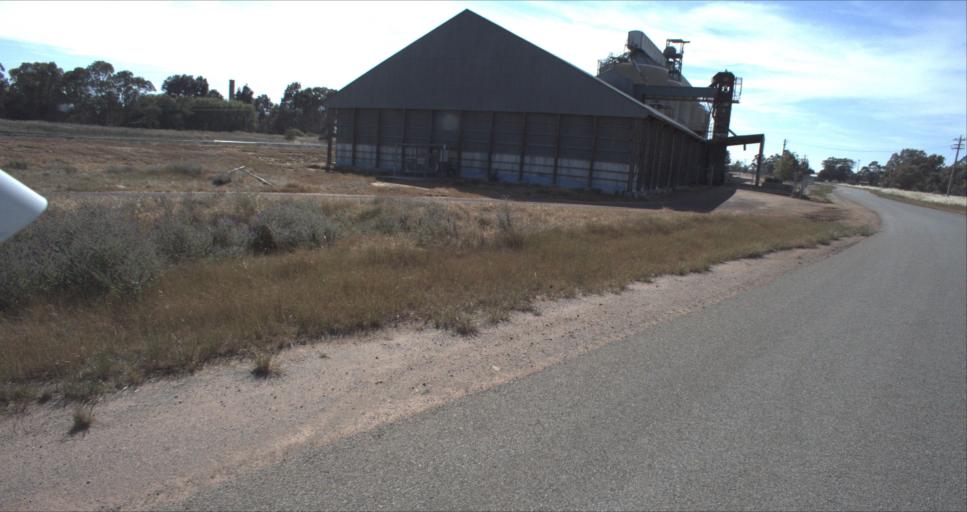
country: AU
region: New South Wales
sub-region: Leeton
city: Leeton
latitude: -34.6047
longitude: 146.4044
